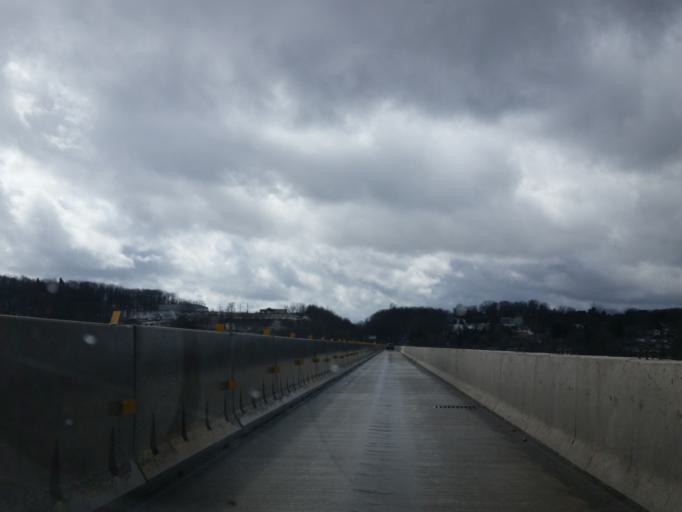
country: US
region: Pennsylvania
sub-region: Lackawanna County
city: Clarks Green
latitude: 41.4849
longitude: -75.6890
